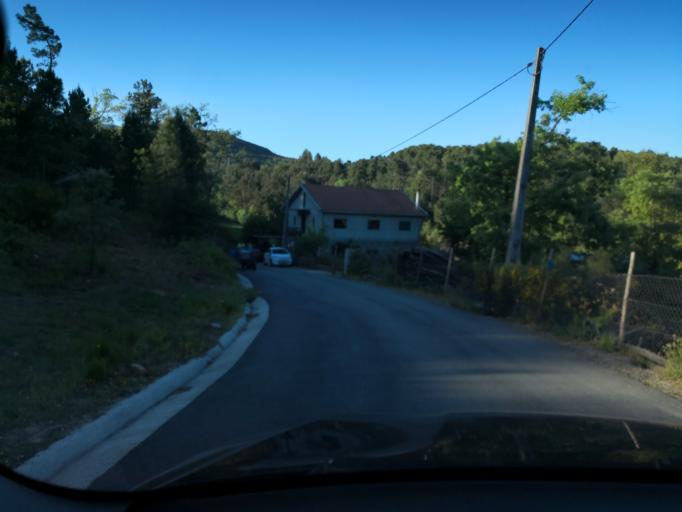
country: PT
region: Vila Real
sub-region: Vila Real
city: Vila Real
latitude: 41.3377
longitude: -7.7347
